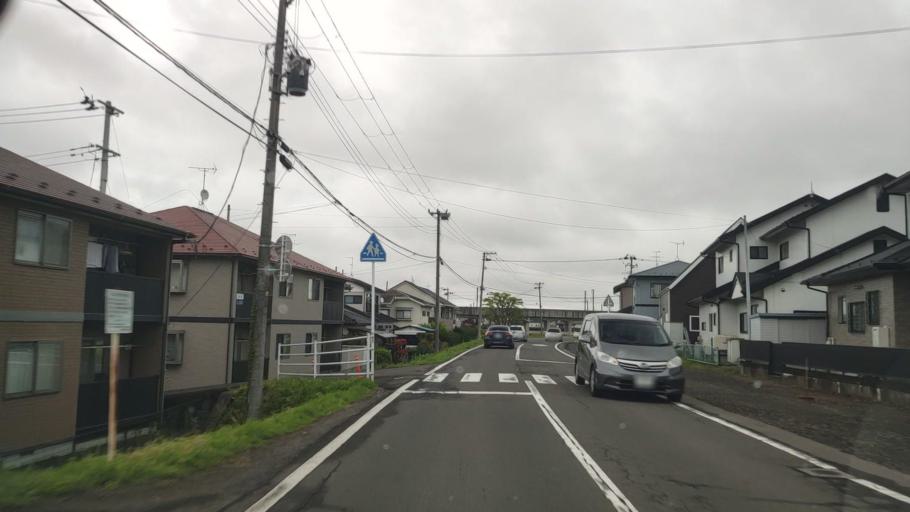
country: JP
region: Miyagi
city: Sendai
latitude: 38.2104
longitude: 140.8799
